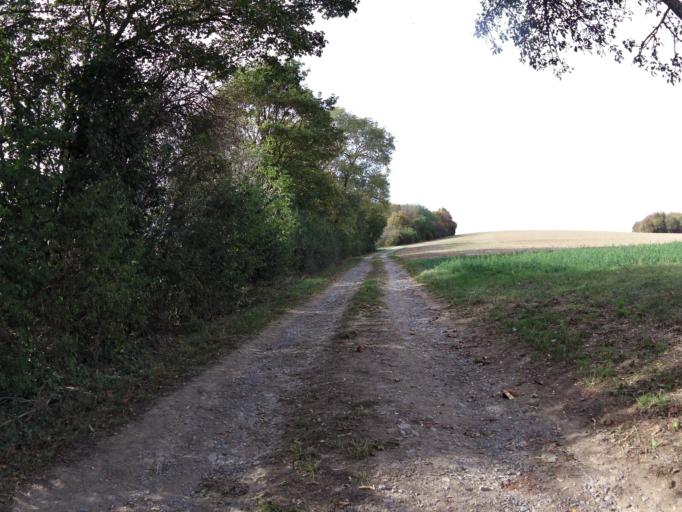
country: DE
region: Bavaria
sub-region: Regierungsbezirk Unterfranken
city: Eibelstadt
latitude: 49.7001
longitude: 9.9644
